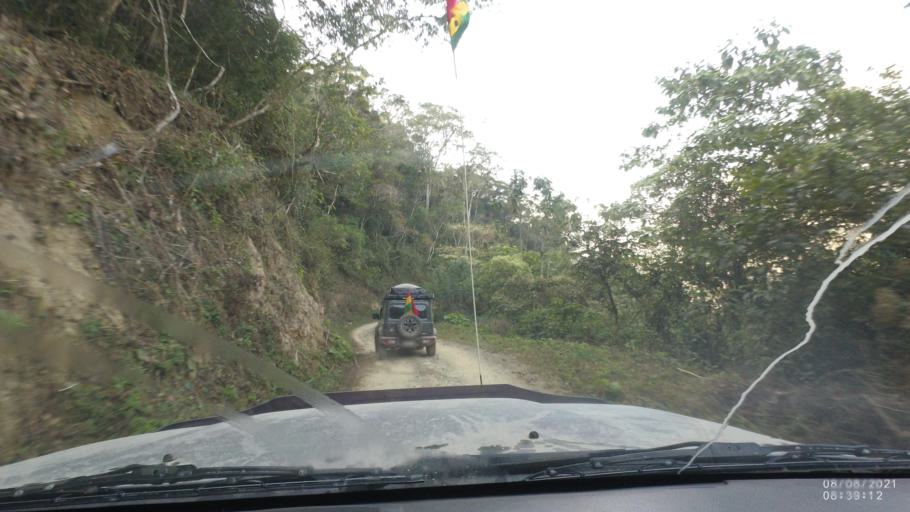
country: BO
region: La Paz
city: Quime
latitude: -16.5273
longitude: -66.7651
